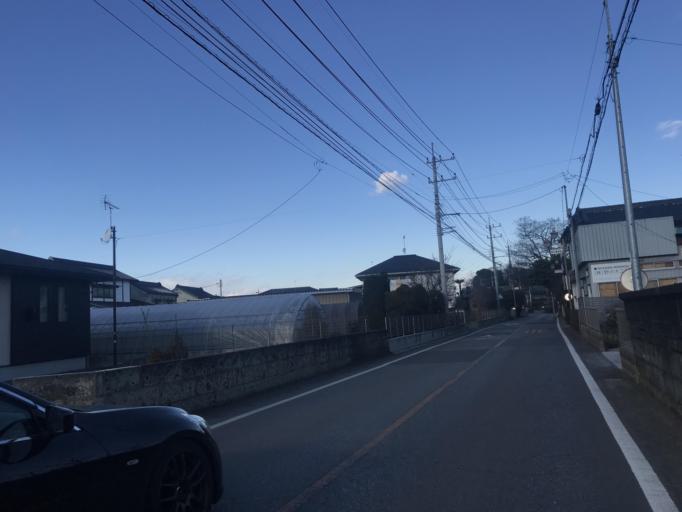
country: JP
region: Tochigi
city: Kaminokawa
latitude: 36.4290
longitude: 139.8708
